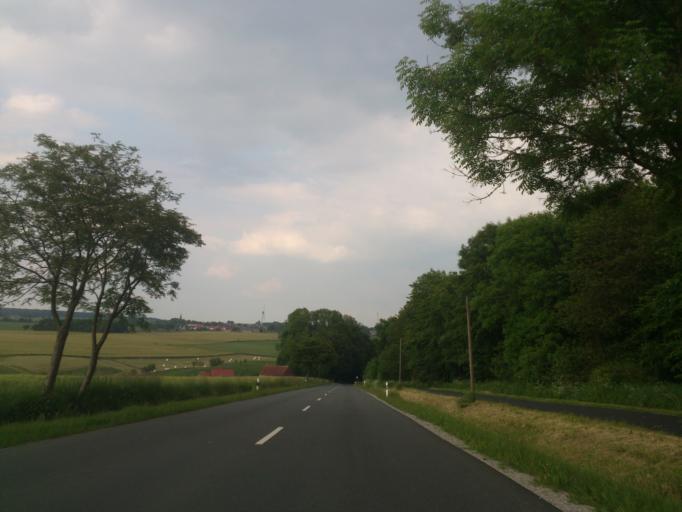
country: DE
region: North Rhine-Westphalia
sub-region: Regierungsbezirk Detmold
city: Paderborn
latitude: 51.6619
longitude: 8.8123
